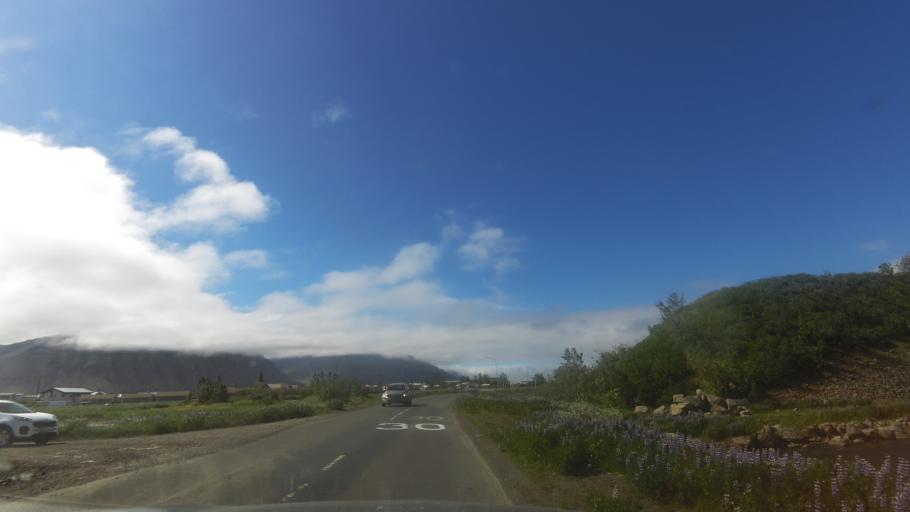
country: IS
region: Westfjords
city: Isafjoerdur
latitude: 66.0513
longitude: -23.5076
